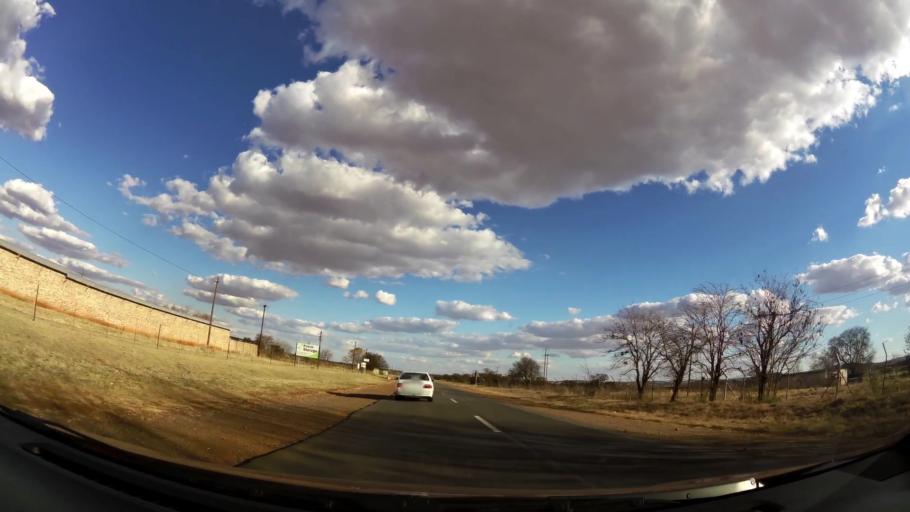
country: ZA
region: North-West
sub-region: Dr Kenneth Kaunda District Municipality
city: Potchefstroom
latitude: -26.6310
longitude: 27.1080
